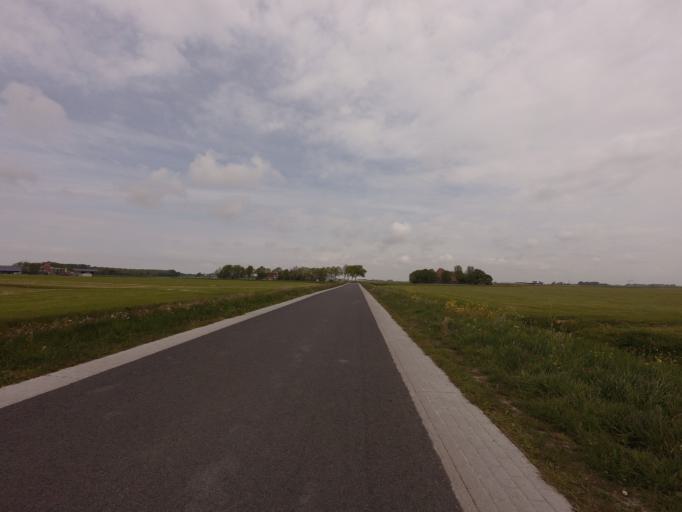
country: NL
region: Friesland
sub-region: Sudwest Fryslan
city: Bolsward
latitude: 53.0860
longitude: 5.4828
